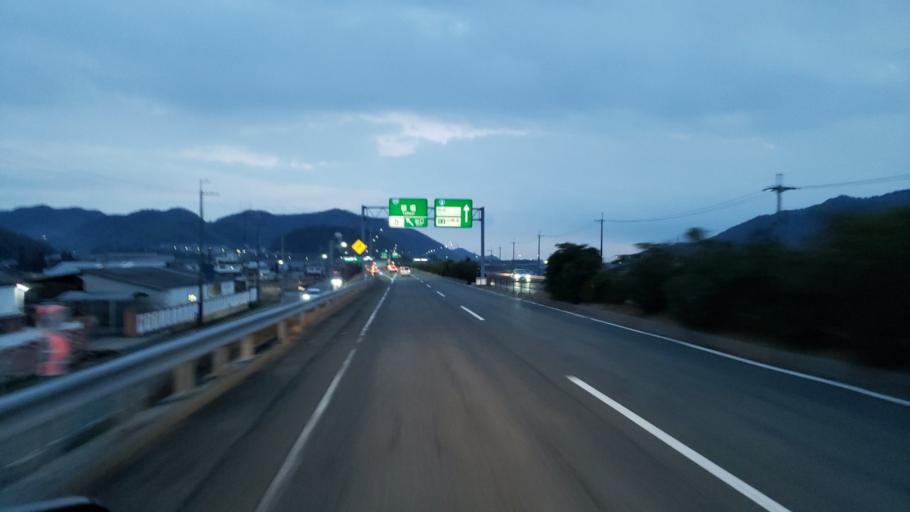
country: JP
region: Hyogo
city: Himeji
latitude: 34.8811
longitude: 134.7413
